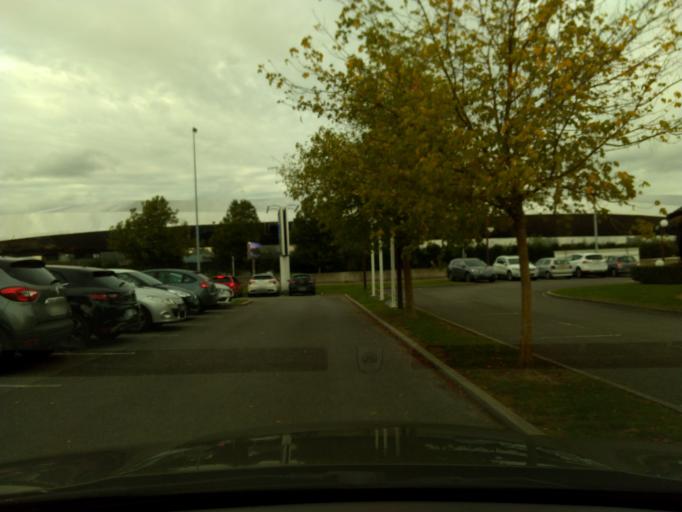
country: FR
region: Lorraine
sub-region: Departement de la Moselle
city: Augny
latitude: 49.0793
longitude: 6.1053
